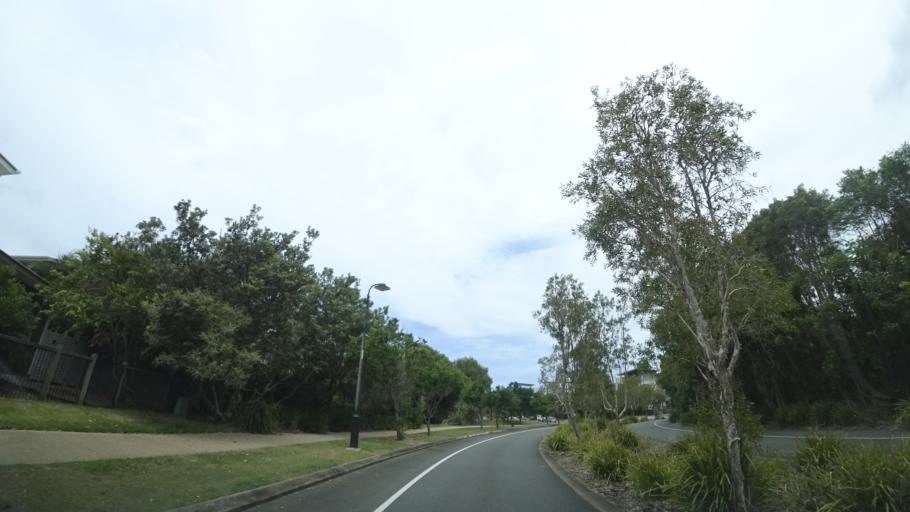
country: AU
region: Queensland
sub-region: Sunshine Coast
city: Coolum Beach
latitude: -26.5693
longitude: 153.0949
